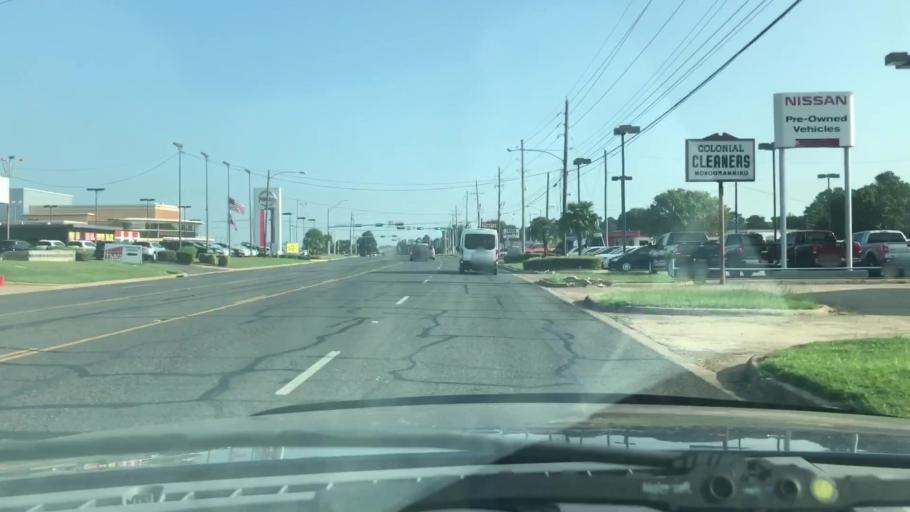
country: US
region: Arkansas
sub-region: Miller County
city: Texarkana
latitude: 33.4523
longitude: -94.0650
